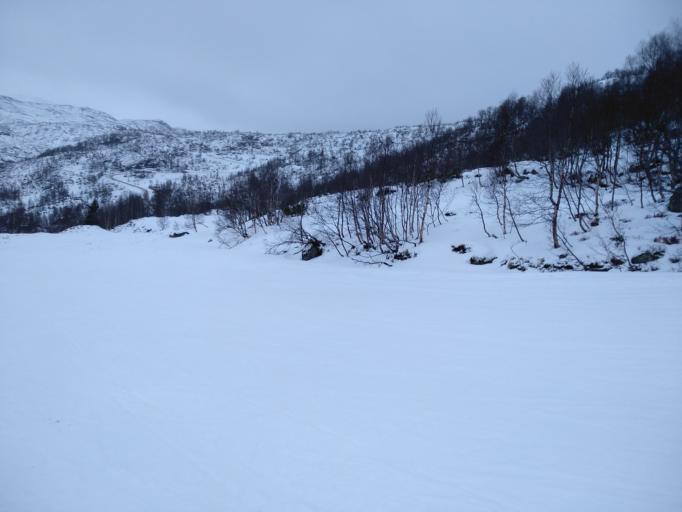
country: NO
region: Vest-Agder
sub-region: Sirdal
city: Tonstad
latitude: 59.0219
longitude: 6.9187
